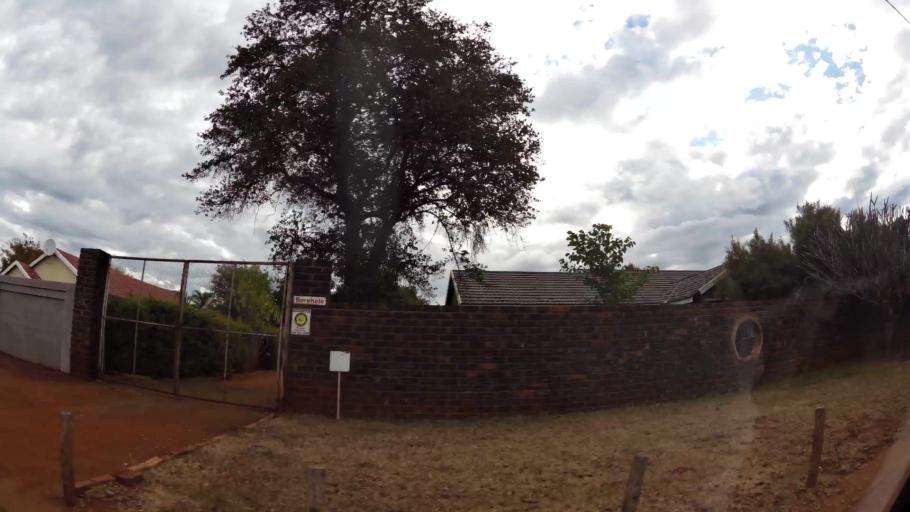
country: ZA
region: Limpopo
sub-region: Waterberg District Municipality
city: Modimolle
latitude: -24.5051
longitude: 28.7249
